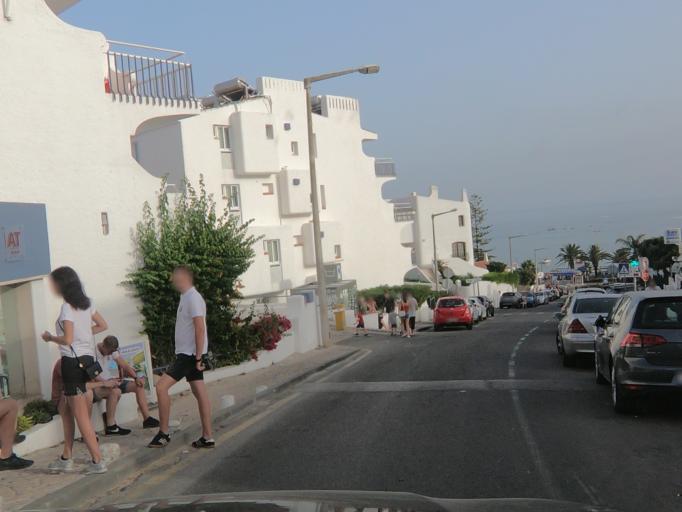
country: PT
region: Faro
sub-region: Albufeira
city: Albufeira
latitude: 37.0880
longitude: -8.2260
